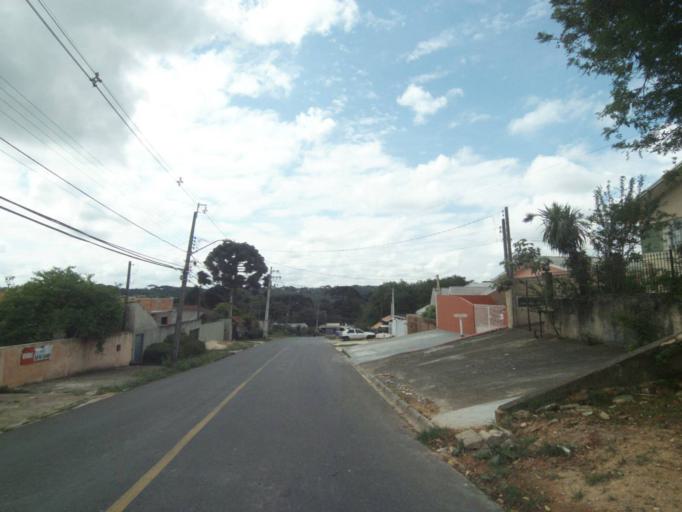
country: BR
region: Parana
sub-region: Curitiba
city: Curitiba
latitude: -25.3803
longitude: -49.2922
